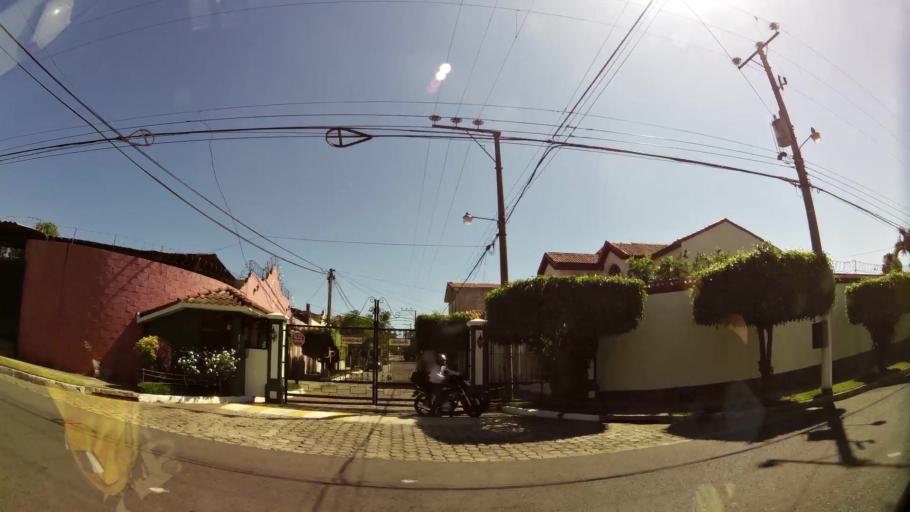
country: SV
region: La Libertad
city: Nuevo Cuscatlan
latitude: 13.6478
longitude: -89.2796
